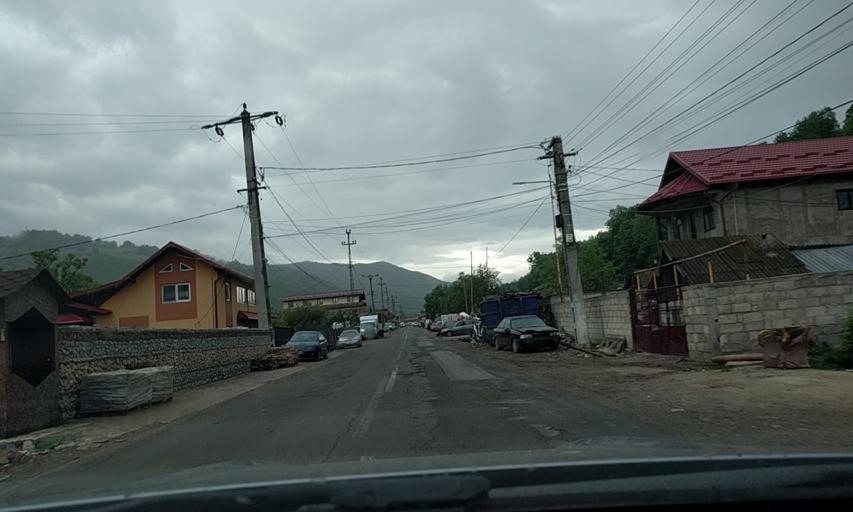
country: RO
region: Dambovita
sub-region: Comuna Moroeni
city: Glod
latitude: 45.2362
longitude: 25.4447
